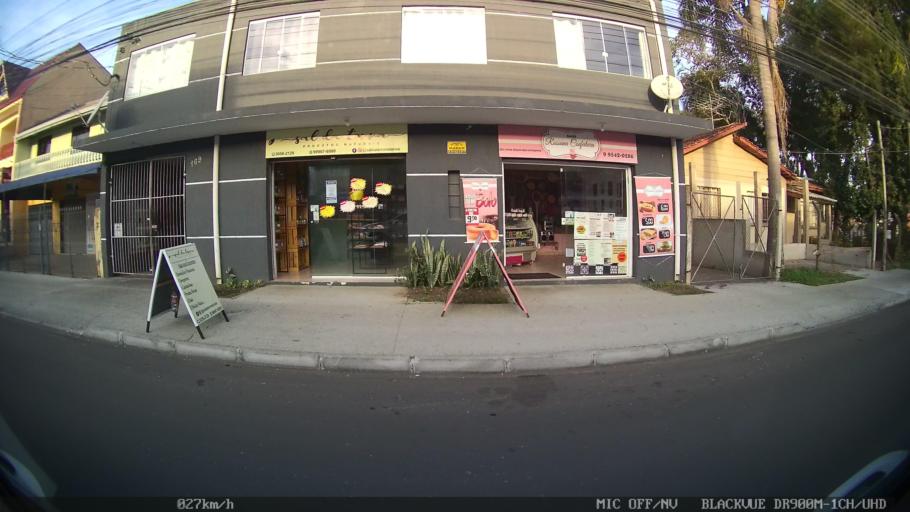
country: BR
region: Parana
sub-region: Pinhais
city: Pinhais
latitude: -25.4407
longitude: -49.1609
